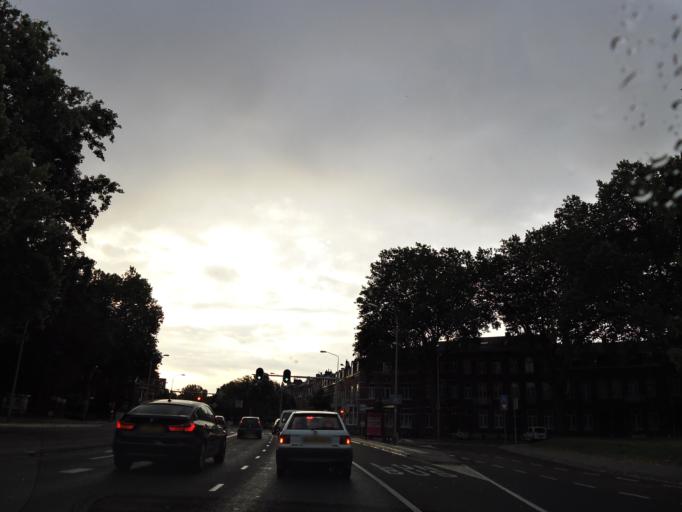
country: NL
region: Limburg
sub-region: Gemeente Maastricht
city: Maastricht
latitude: 50.8417
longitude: 5.6878
